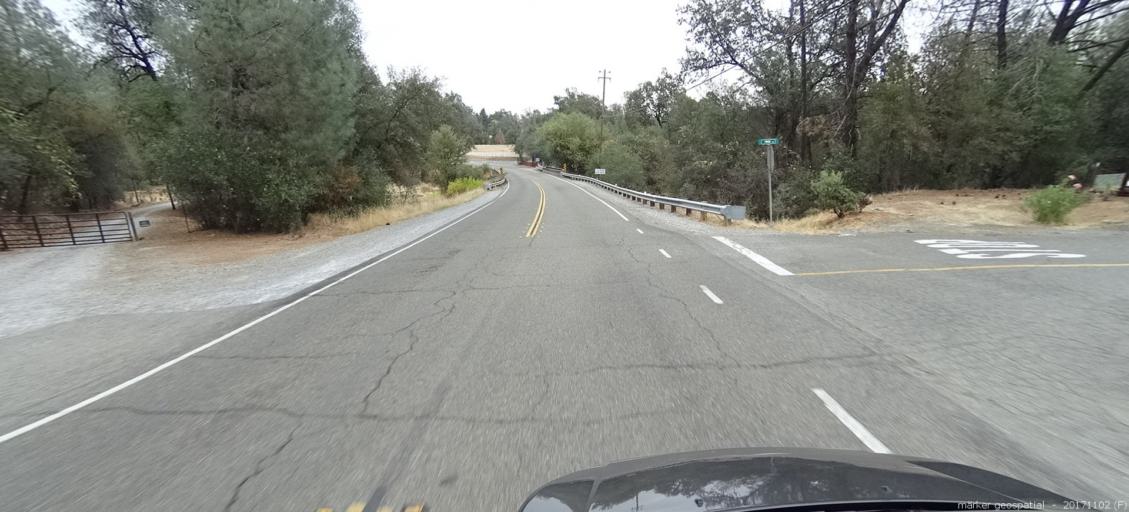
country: US
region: California
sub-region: Shasta County
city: Shasta Lake
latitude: 40.6766
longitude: -122.3038
